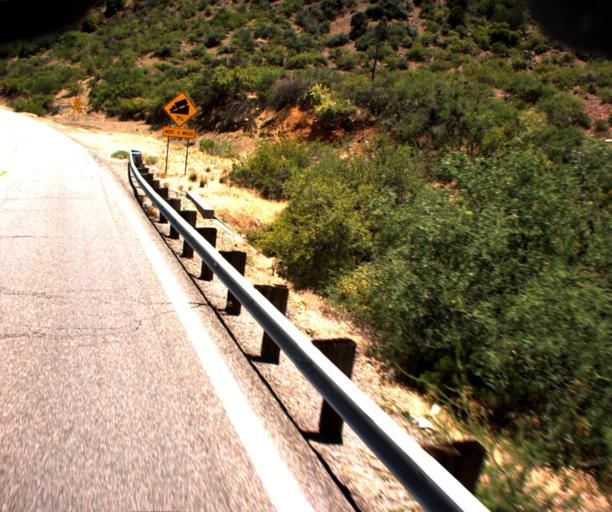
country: US
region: Arizona
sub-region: Pinal County
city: Kearny
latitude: 33.1959
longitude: -110.8050
